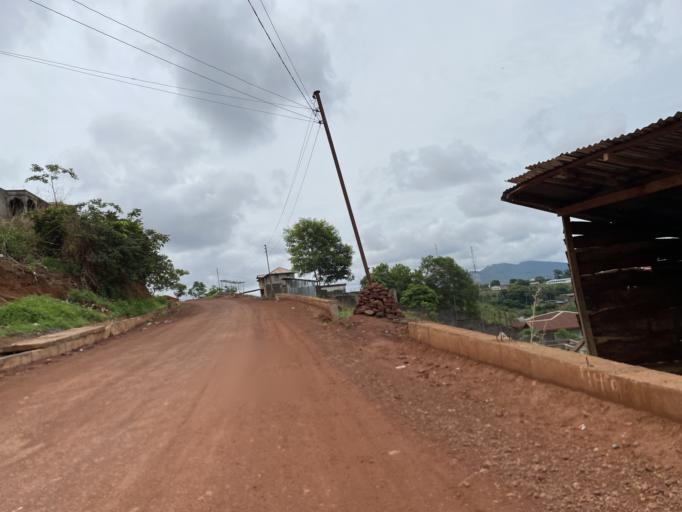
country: SL
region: Western Area
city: Hastings
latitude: 8.3987
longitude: -13.1497
